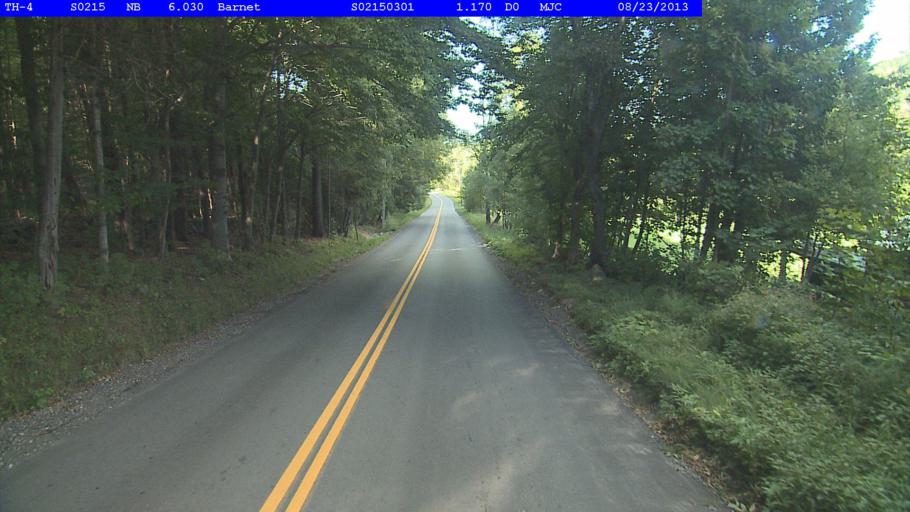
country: US
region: New Hampshire
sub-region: Grafton County
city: Woodsville
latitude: 44.2900
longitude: -72.1668
